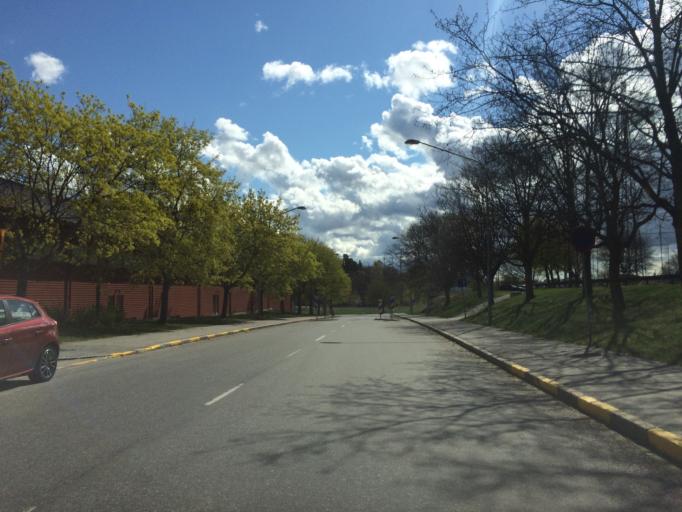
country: SE
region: Stockholm
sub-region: Huddinge Kommun
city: Segeltorp
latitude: 59.2896
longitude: 17.9261
